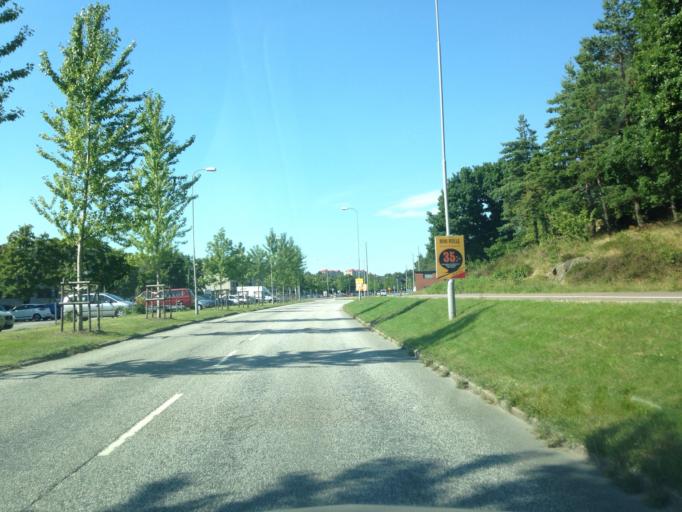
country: SE
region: Vaestra Goetaland
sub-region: Goteborg
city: Majorna
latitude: 57.7227
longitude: 11.9026
